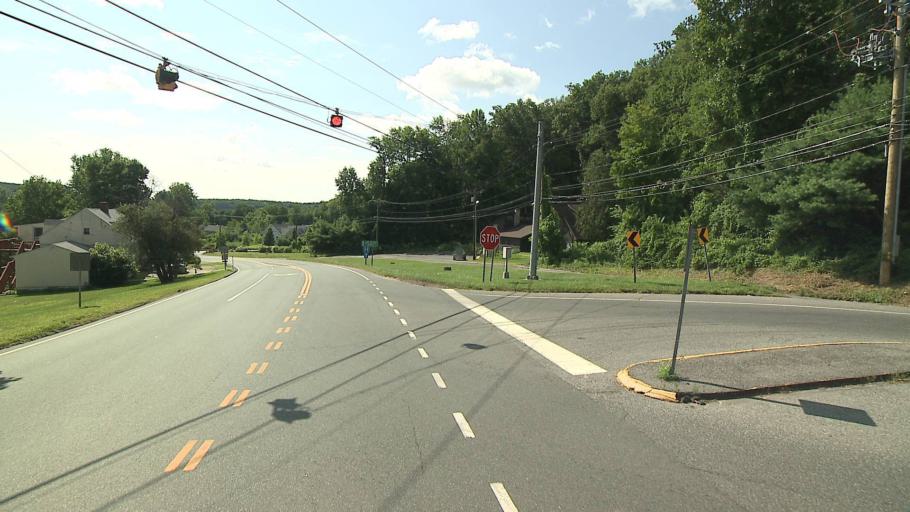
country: US
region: Connecticut
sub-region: Fairfield County
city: Sherman
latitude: 41.5950
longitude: -73.4571
